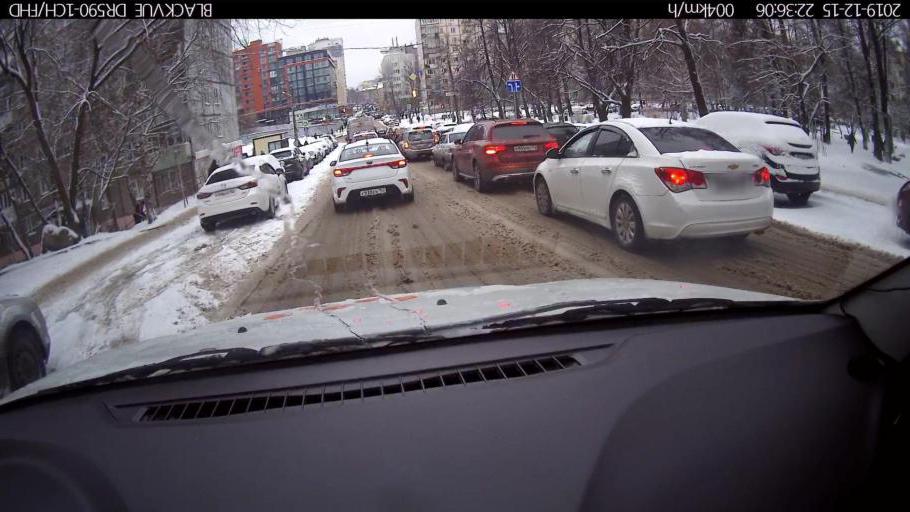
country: RU
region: Nizjnij Novgorod
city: Nizhniy Novgorod
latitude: 56.3222
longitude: 44.0185
